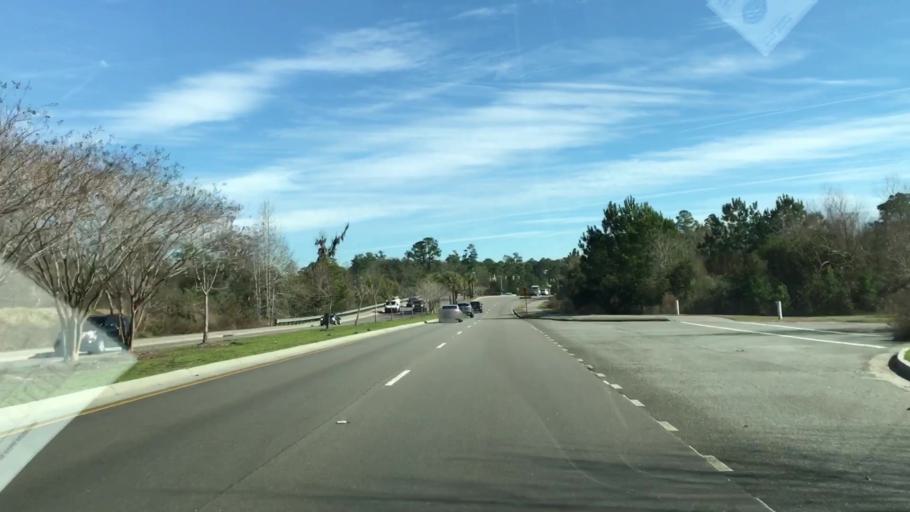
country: US
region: South Carolina
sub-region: Beaufort County
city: Bluffton
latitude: 32.2623
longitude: -80.8740
